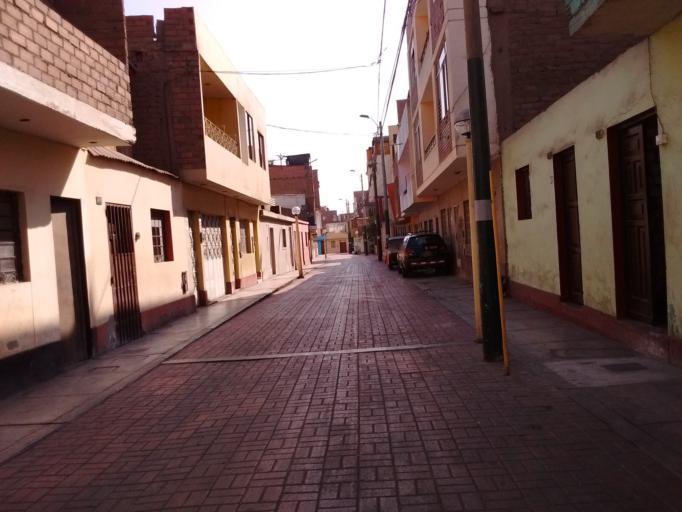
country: PE
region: Callao
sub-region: Callao
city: Callao
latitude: -12.0391
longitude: -77.0838
